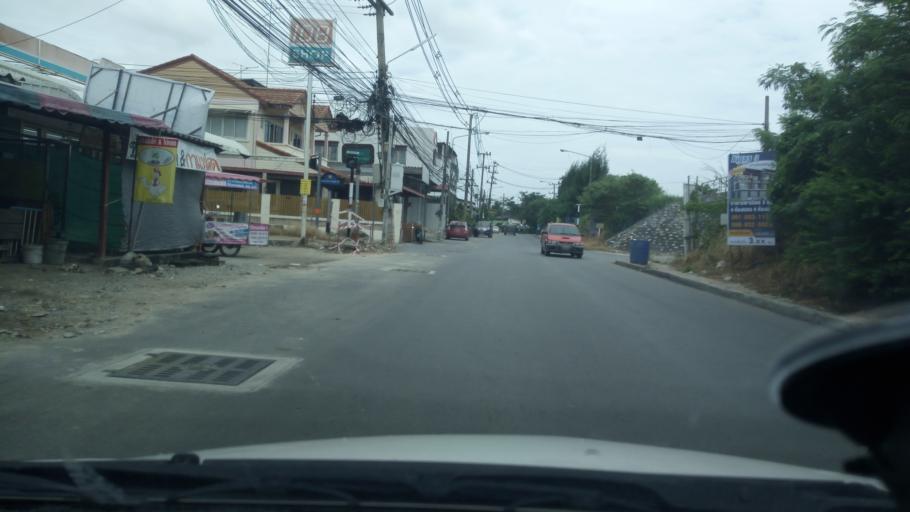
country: TH
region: Chon Buri
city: Chon Buri
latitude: 13.3501
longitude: 101.0060
